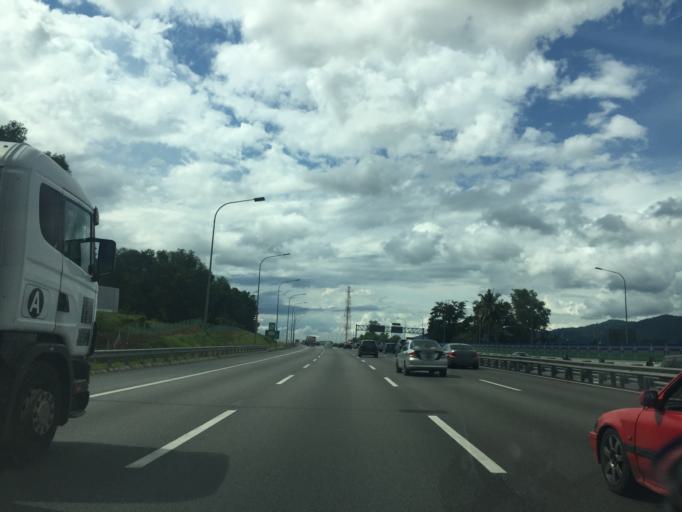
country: MY
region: Negeri Sembilan
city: Seremban
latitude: 2.7183
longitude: 101.9129
